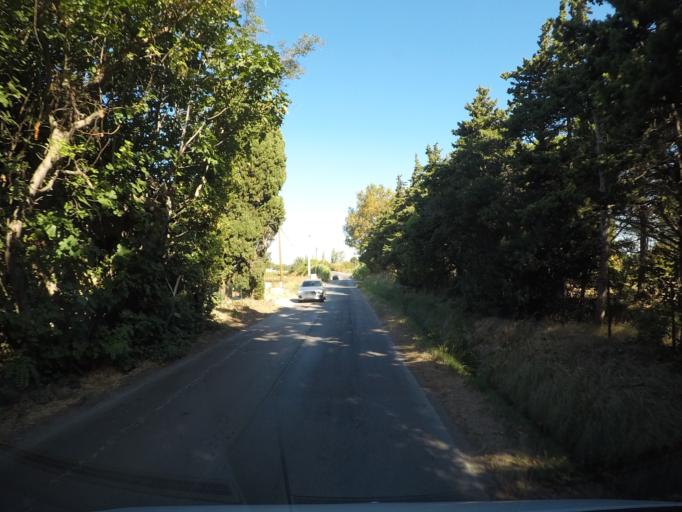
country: FR
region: Languedoc-Roussillon
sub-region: Departement de l'Aude
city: Narbonne
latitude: 43.1702
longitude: 3.0088
